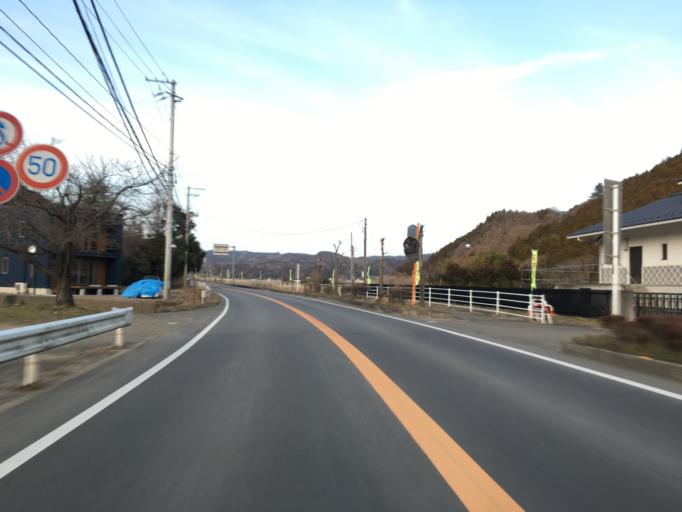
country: JP
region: Ibaraki
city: Daigo
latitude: 36.8556
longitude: 140.4095
